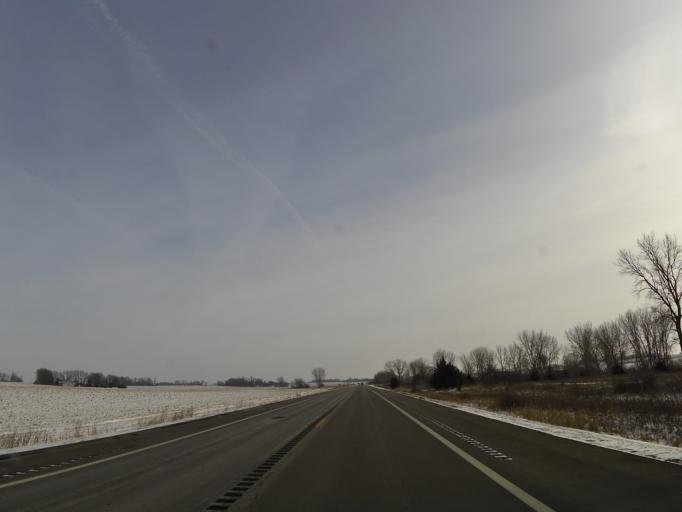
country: US
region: Minnesota
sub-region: McLeod County
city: Hutchinson
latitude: 44.9162
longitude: -94.4595
